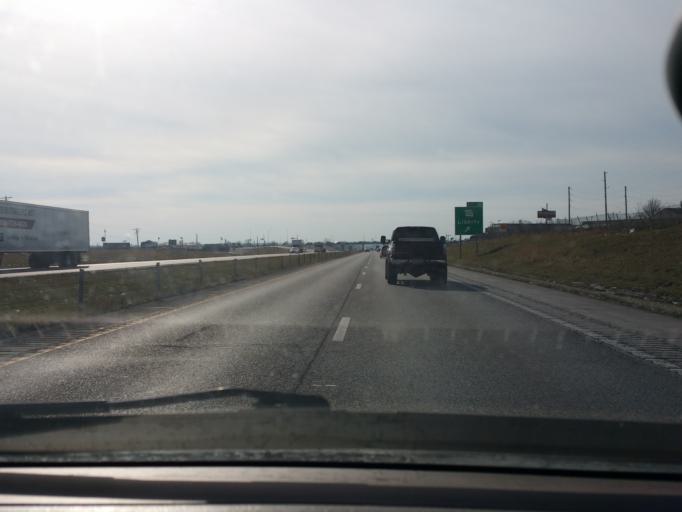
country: US
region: Missouri
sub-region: Clay County
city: Liberty
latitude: 39.2499
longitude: -94.4524
